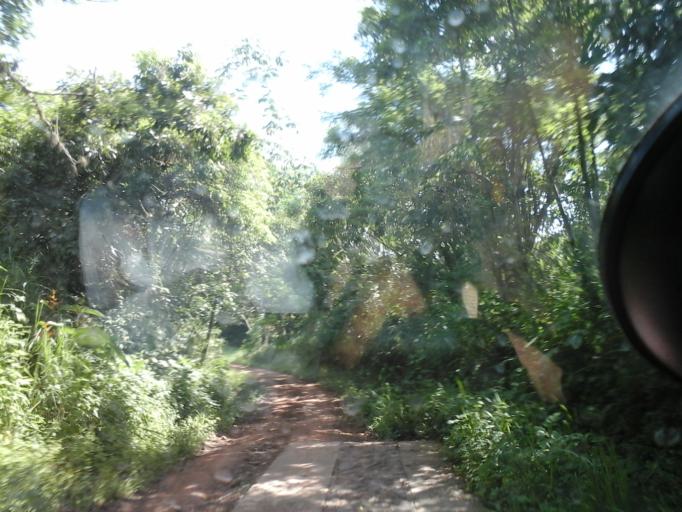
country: CO
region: Cesar
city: San Diego
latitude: 10.2718
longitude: -73.0921
